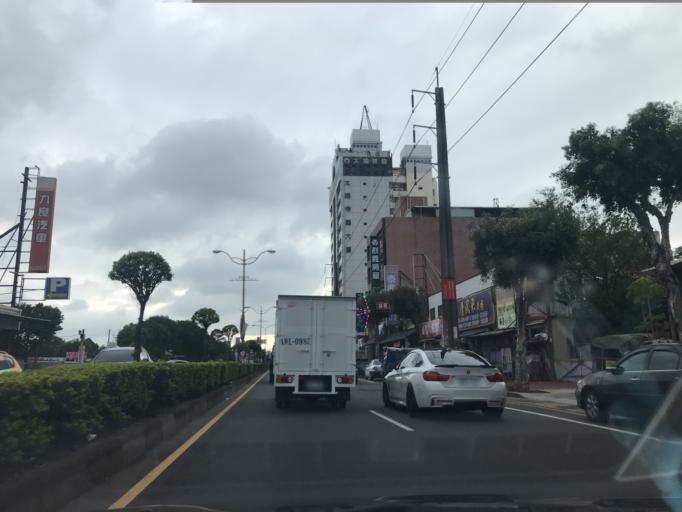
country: TW
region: Taiwan
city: Taoyuan City
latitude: 24.9550
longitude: 121.2452
